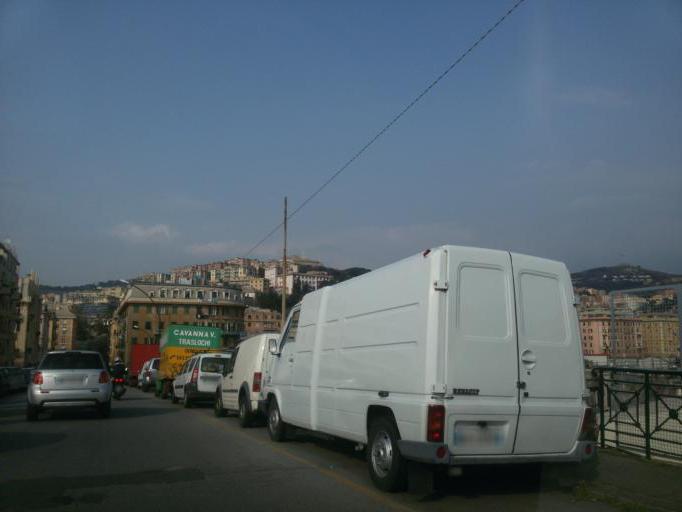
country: IT
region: Liguria
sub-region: Provincia di Genova
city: Genoa
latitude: 44.4052
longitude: 8.9591
